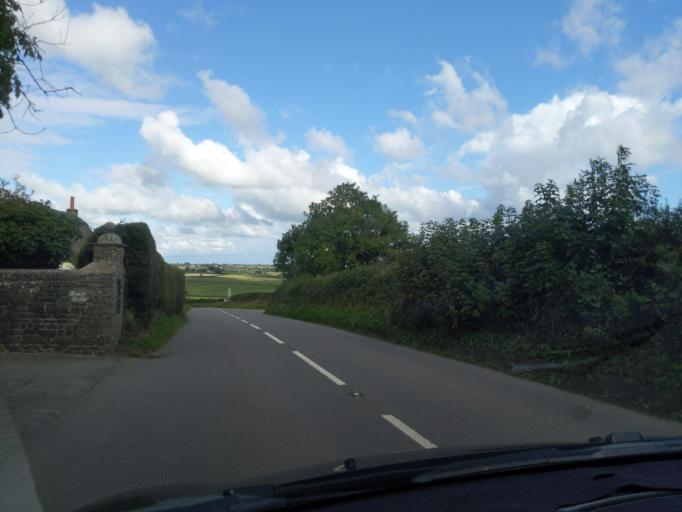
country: GB
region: England
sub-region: Devon
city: Holsworthy
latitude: 50.8837
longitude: -4.2830
